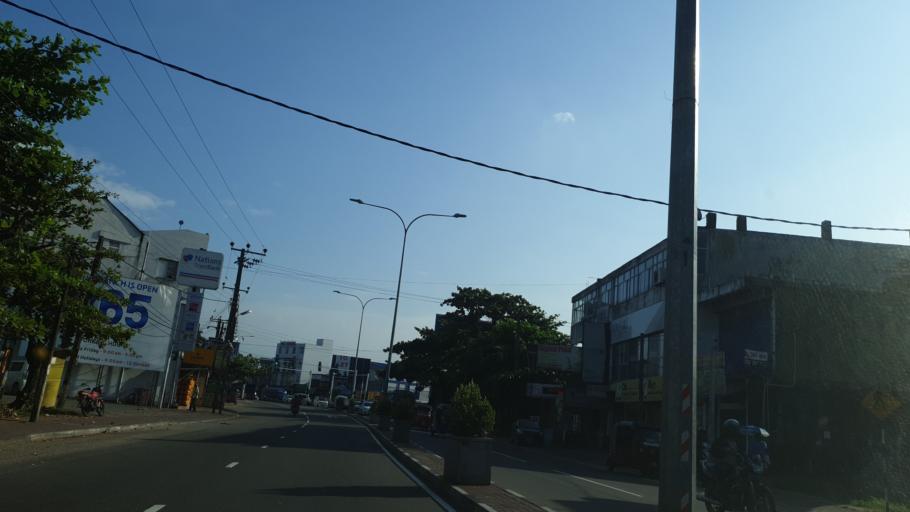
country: LK
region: Western
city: Battaramulla South
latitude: 6.8775
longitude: 79.9352
